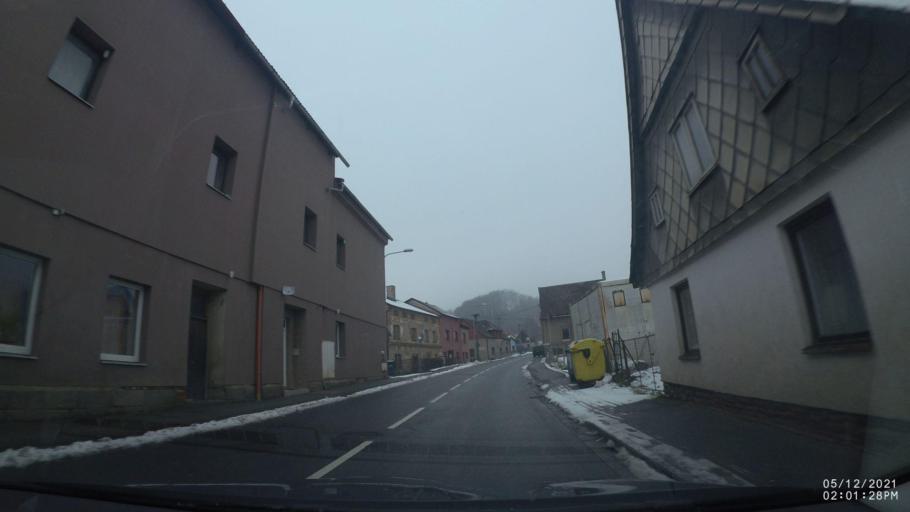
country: CZ
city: Hronov
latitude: 50.4824
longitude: 16.1545
